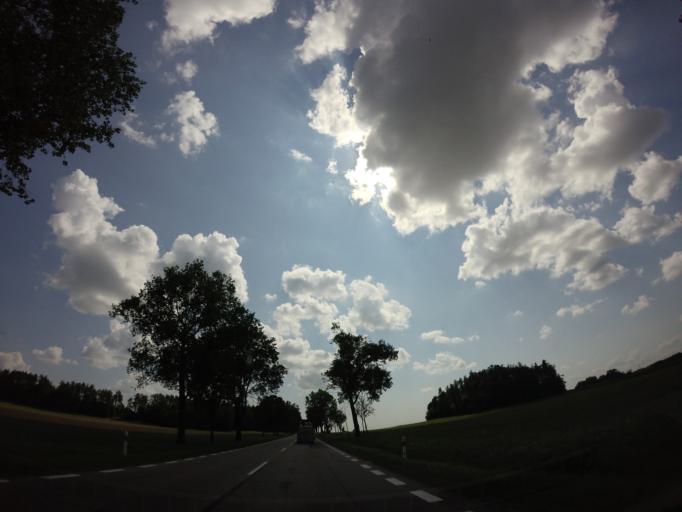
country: PL
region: Podlasie
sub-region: Powiat lomzynski
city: Piatnica
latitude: 53.2706
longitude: 22.1314
